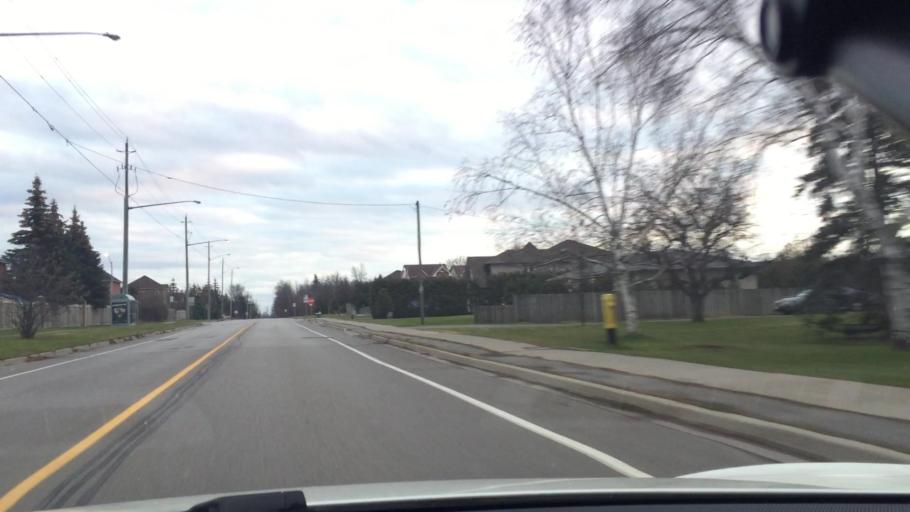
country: CA
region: Ontario
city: Oshawa
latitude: 43.9040
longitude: -78.7853
